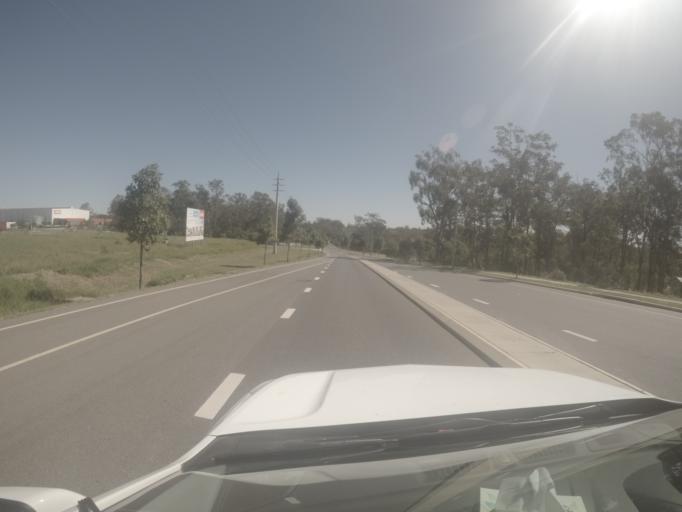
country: AU
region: Queensland
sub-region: Brisbane
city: Wacol
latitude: -27.5852
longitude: 152.9406
